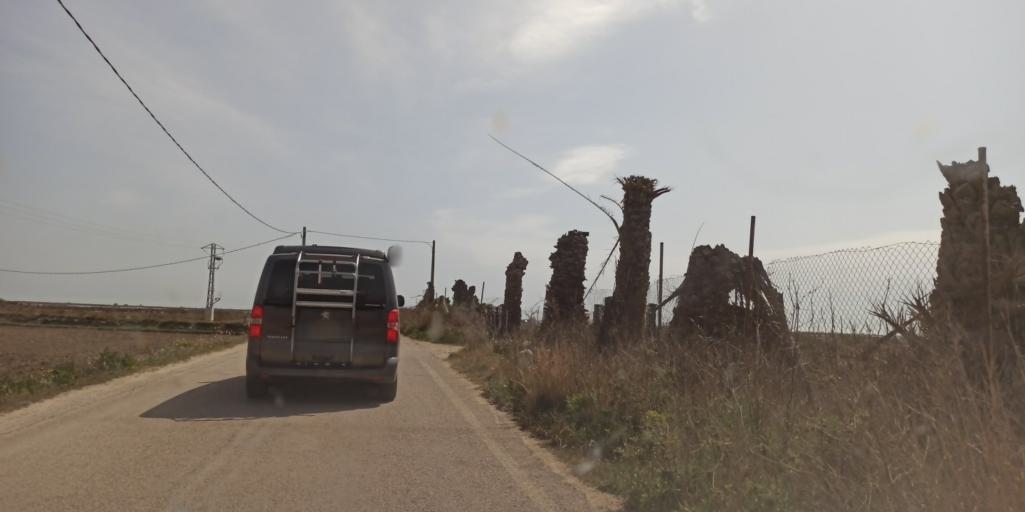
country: ES
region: Catalonia
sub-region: Provincia de Tarragona
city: Deltebre
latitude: 40.6426
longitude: 0.7357
